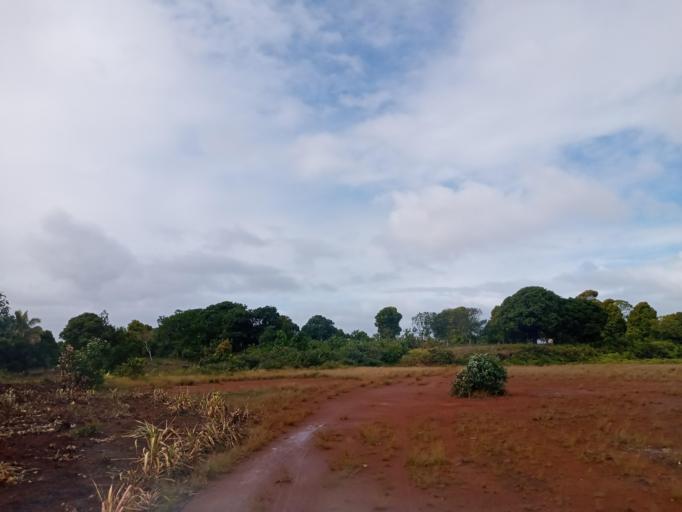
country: MG
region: Atsimo-Atsinanana
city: Vohipaho
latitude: -23.7934
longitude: 47.5503
